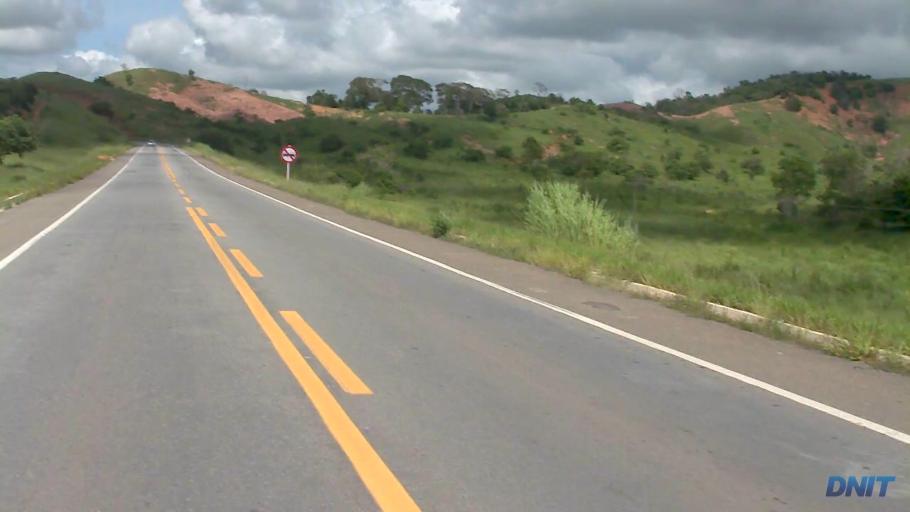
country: BR
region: Minas Gerais
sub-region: Belo Oriente
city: Belo Oriente
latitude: -19.1196
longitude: -42.2131
